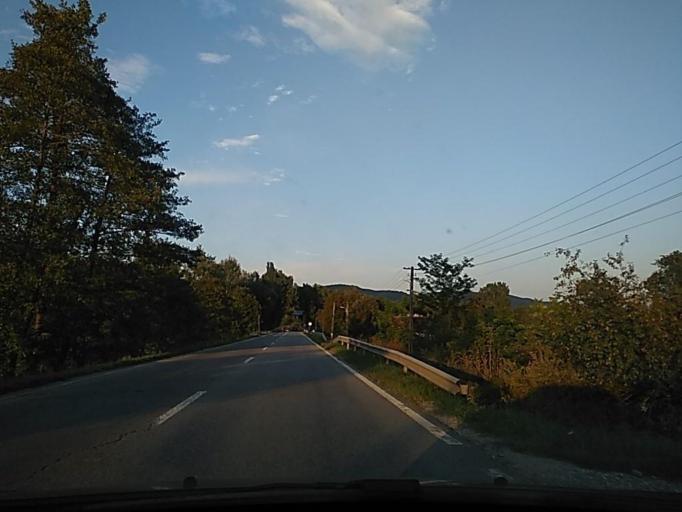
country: RO
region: Valcea
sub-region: Comuna Stoenesti
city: Stoenesti
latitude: 45.1147
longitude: 24.1653
